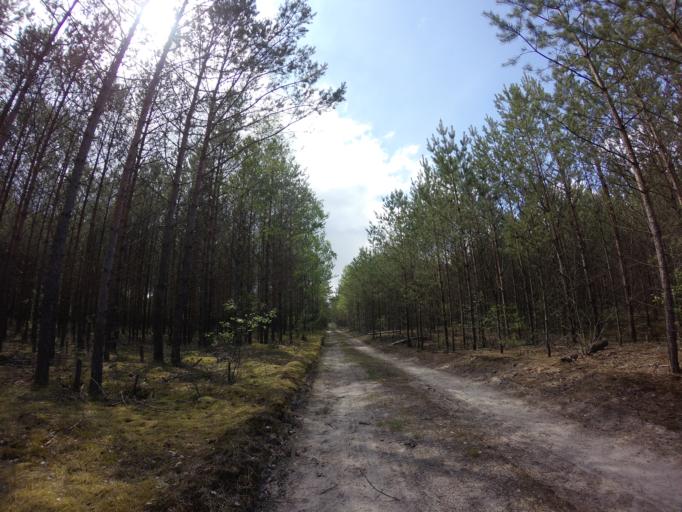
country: PL
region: West Pomeranian Voivodeship
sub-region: Powiat drawski
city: Kalisz Pomorski
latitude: 53.1921
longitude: 15.9695
